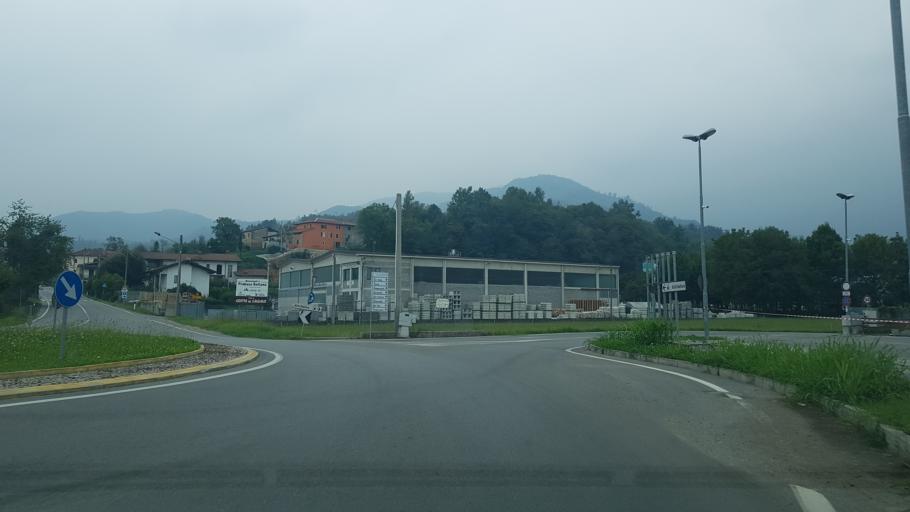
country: IT
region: Piedmont
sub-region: Provincia di Cuneo
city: Villanova Mondovi
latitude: 44.3402
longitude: 7.7778
